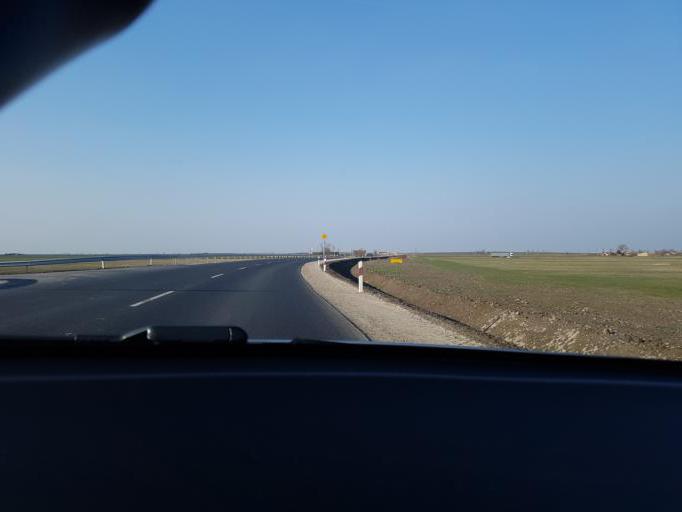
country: RO
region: Arad
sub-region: Comuna Nadlac
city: Nadlac
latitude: 46.1932
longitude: 20.7135
